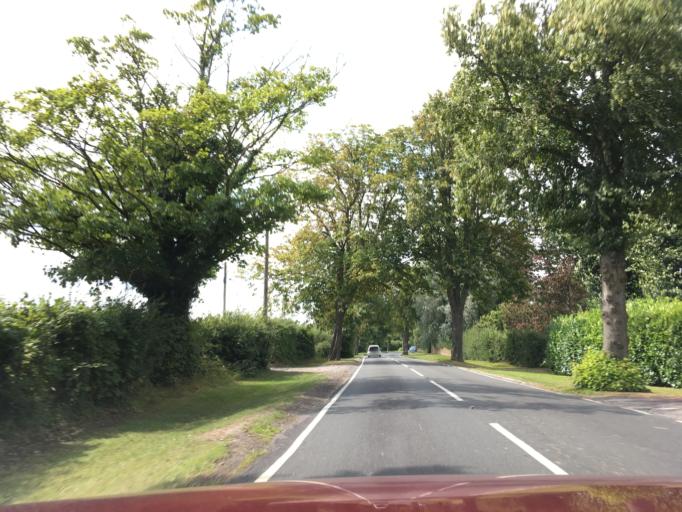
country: GB
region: England
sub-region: Kent
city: Tenterden
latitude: 51.0657
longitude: 0.7103
